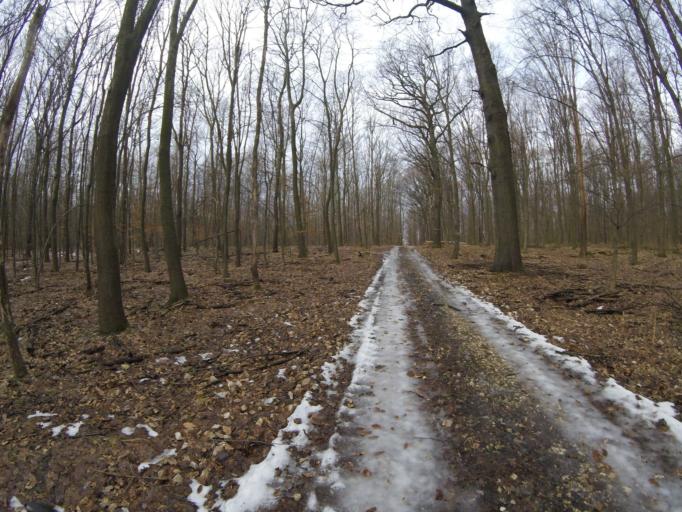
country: HU
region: Komarom-Esztergom
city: Kesztolc
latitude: 47.7215
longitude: 18.8272
